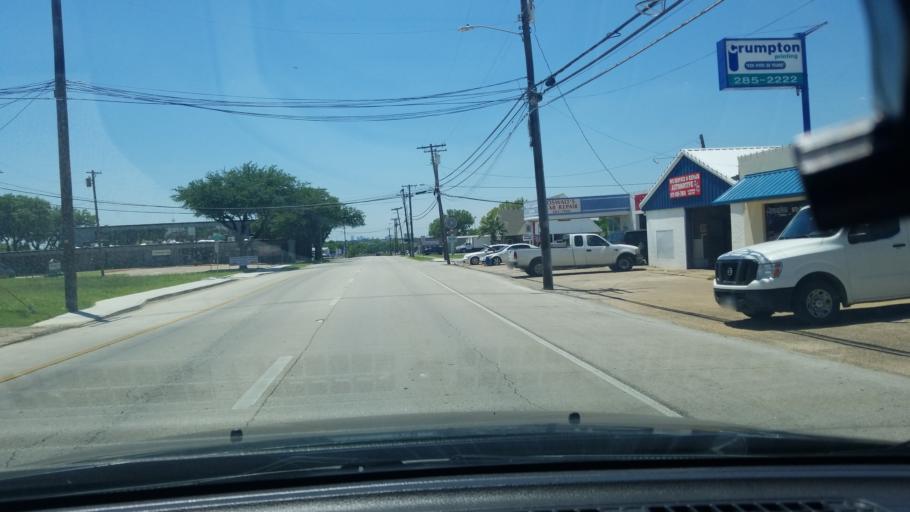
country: US
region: Texas
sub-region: Dallas County
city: Mesquite
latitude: 32.7670
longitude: -96.6015
